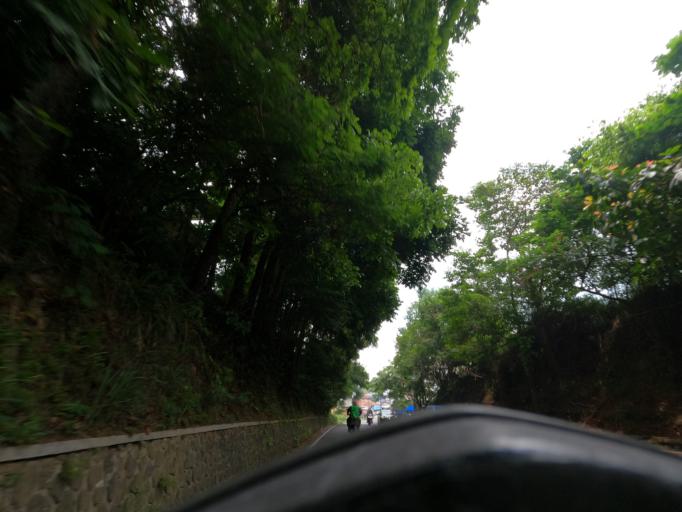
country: ID
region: West Java
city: Sukabumi
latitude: -6.7563
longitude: 107.0465
